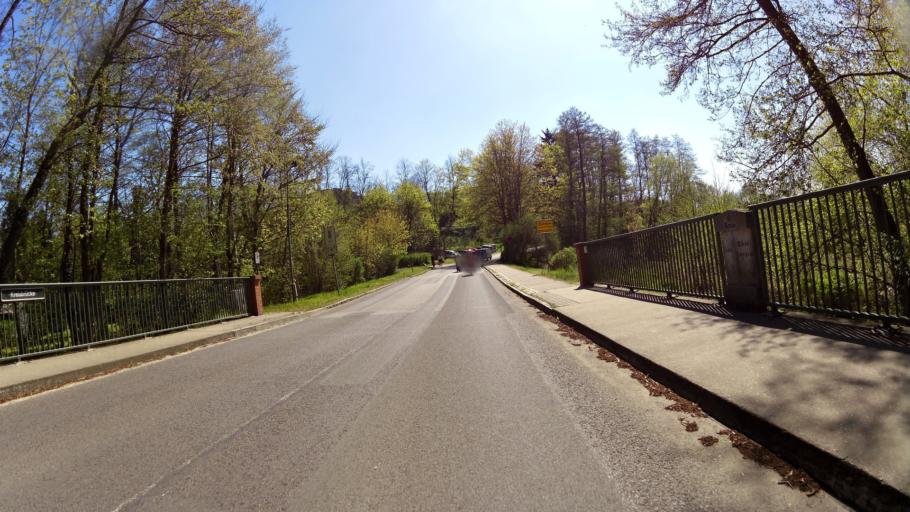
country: DE
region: Brandenburg
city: Buckow
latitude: 52.5776
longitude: 14.0695
